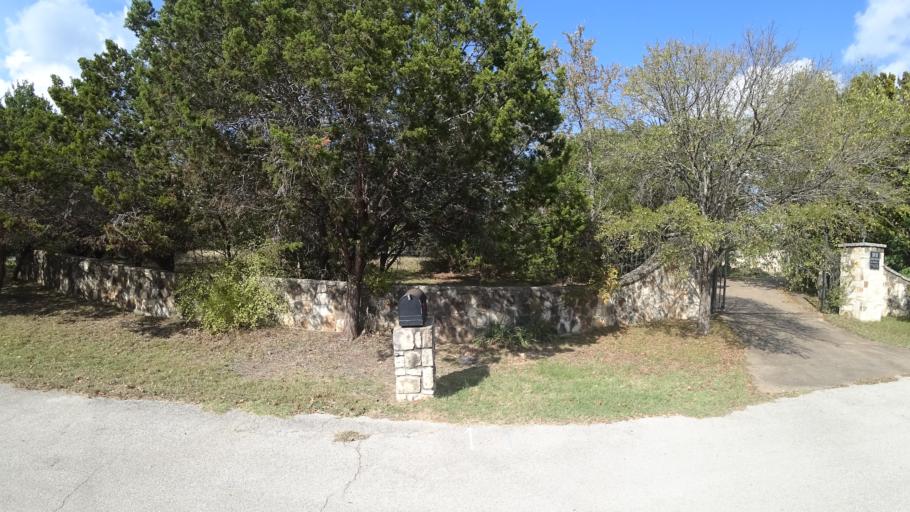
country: US
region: Texas
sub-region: Travis County
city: Barton Creek
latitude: 30.2991
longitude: -97.8622
